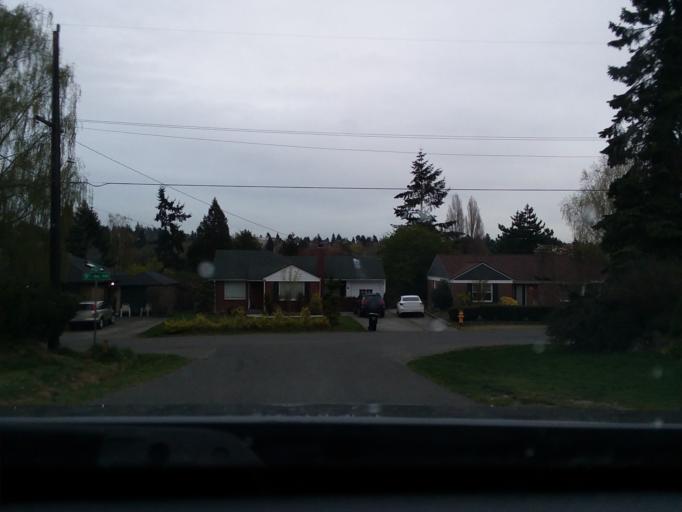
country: US
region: Washington
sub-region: King County
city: Shoreline
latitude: 47.7034
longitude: -122.3691
